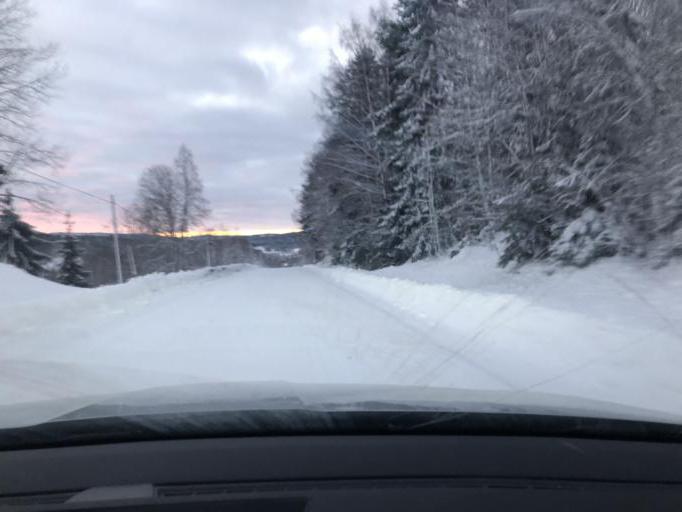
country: SE
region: Vaesternorrland
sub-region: Kramfors Kommun
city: Nordingra
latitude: 62.9272
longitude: 18.1340
